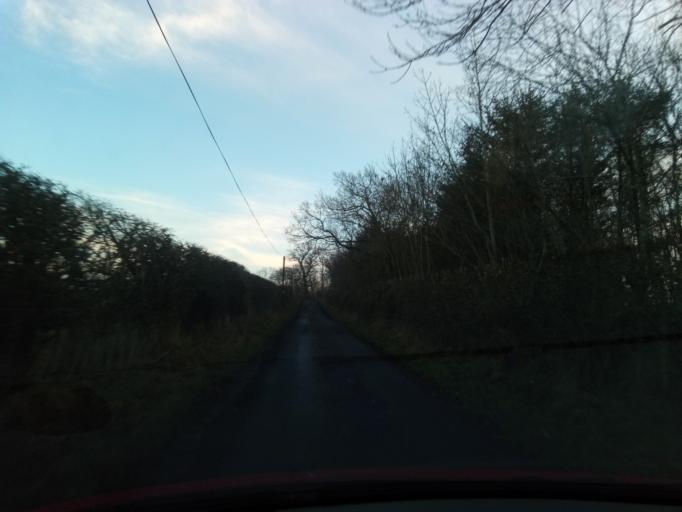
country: GB
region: Scotland
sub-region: The Scottish Borders
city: Saint Boswells
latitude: 55.5251
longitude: -2.6595
